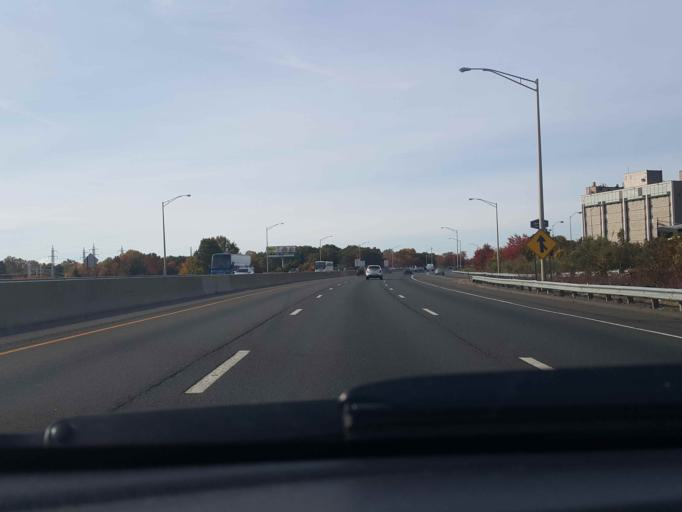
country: US
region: Connecticut
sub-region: New Haven County
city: West Haven
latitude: 41.2703
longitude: -72.9724
